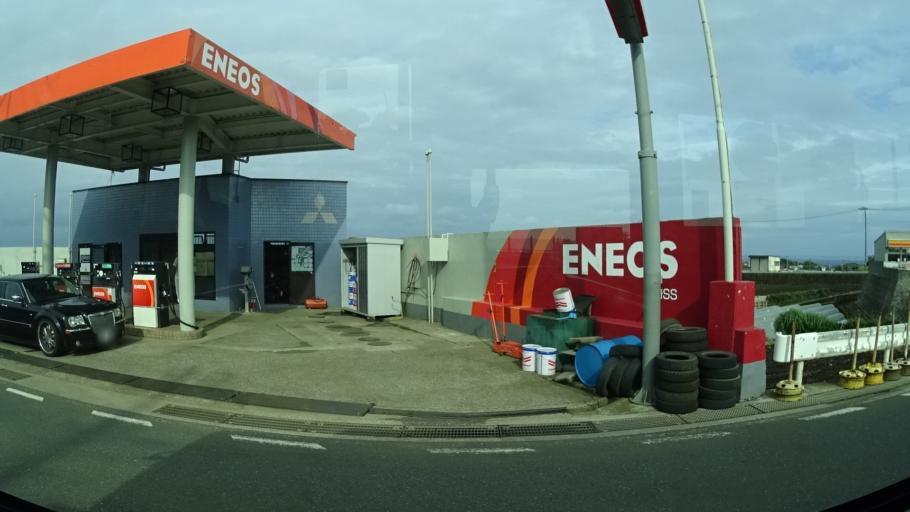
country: JP
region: Kanagawa
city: Miura
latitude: 35.1534
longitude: 139.6687
